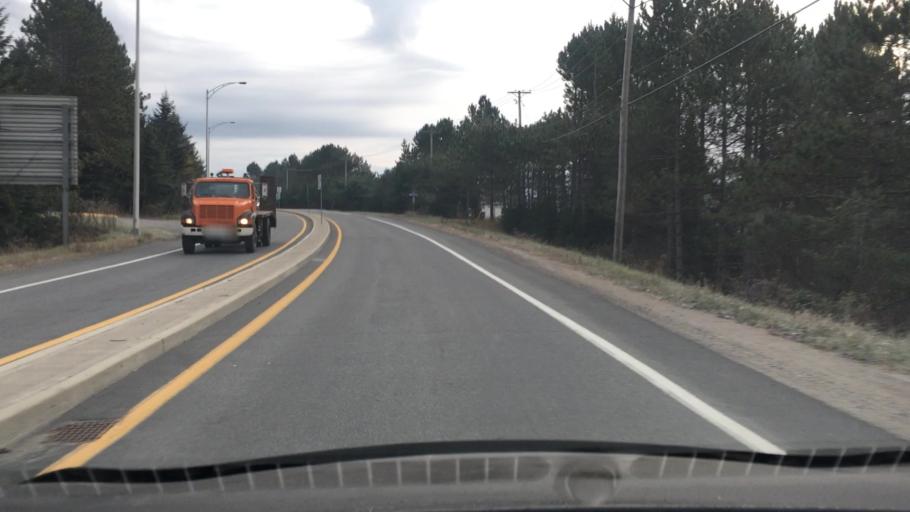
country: CA
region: Quebec
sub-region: Laurentides
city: Saint-Sauveur
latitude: 45.9030
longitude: -74.2434
